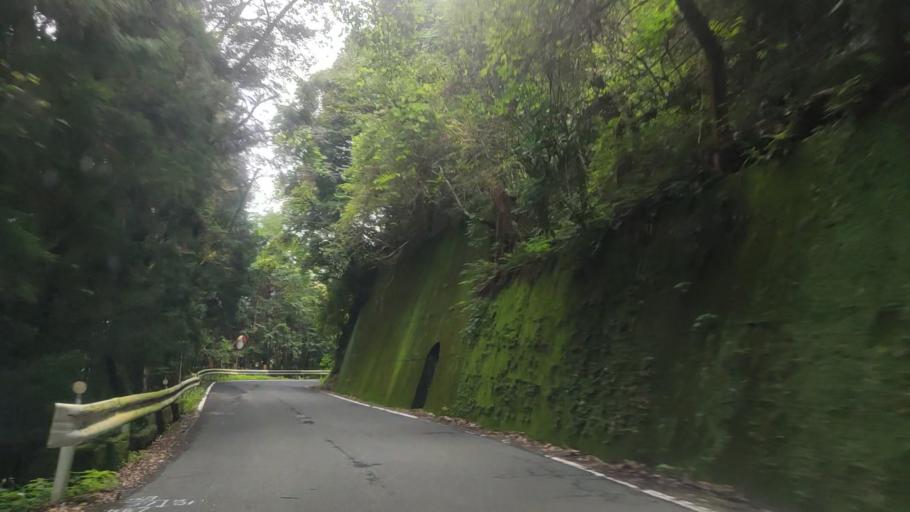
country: JP
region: Wakayama
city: Koya
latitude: 34.2501
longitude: 135.5451
